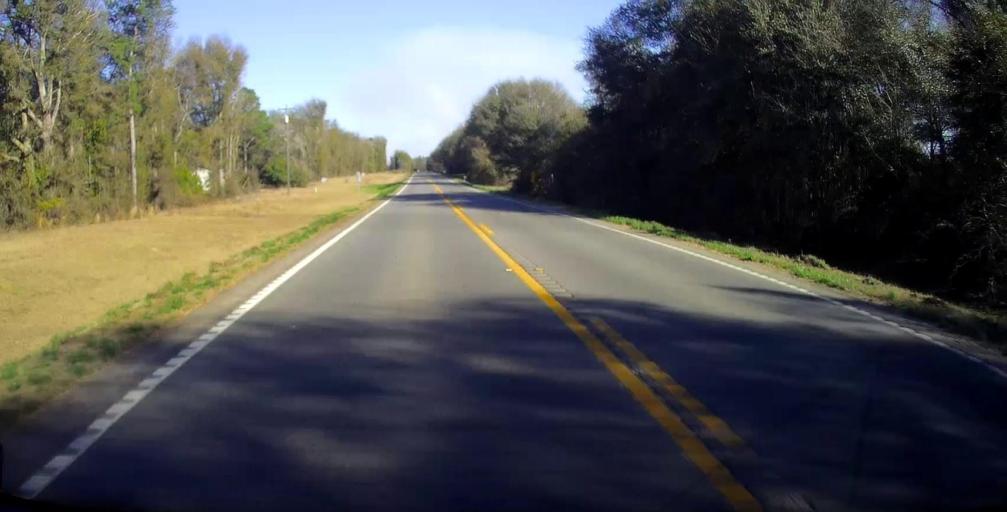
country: US
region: Georgia
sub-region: Macon County
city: Oglethorpe
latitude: 32.3318
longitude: -84.1006
